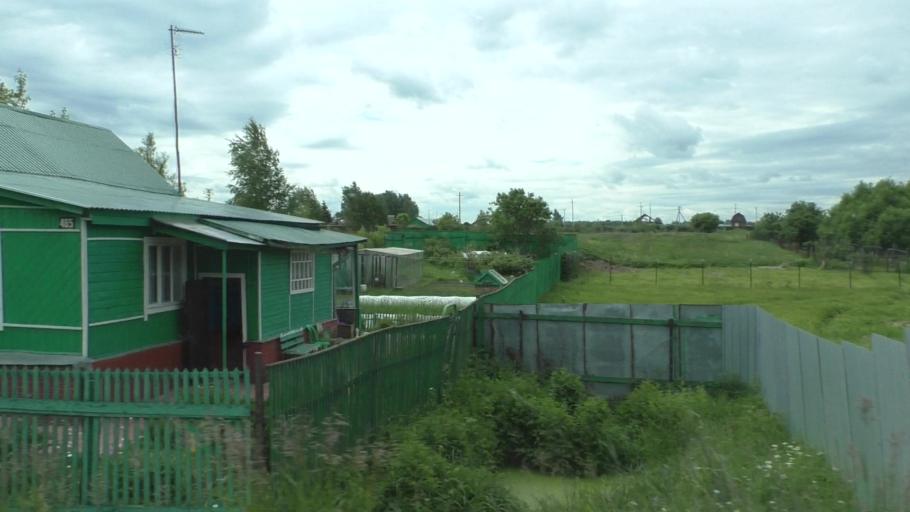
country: RU
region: Moskovskaya
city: Imeni Tsyurupy
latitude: 55.5075
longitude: 38.7654
